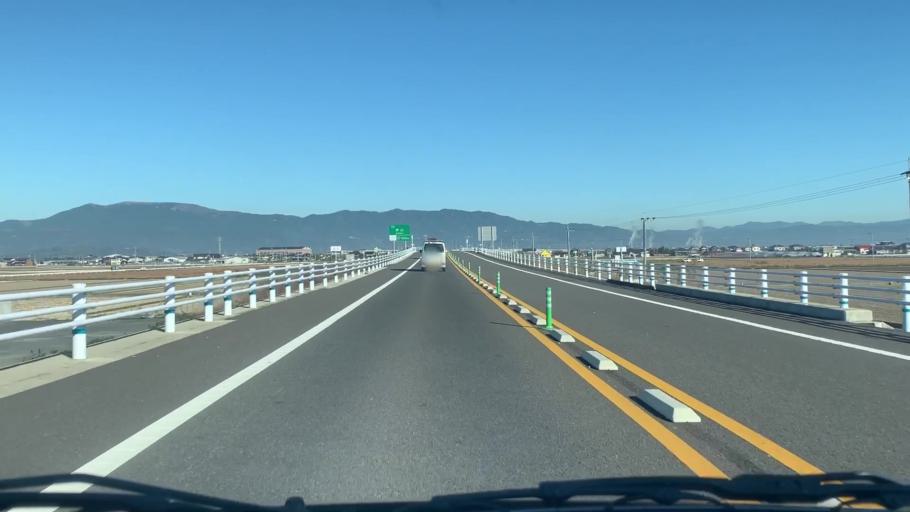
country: JP
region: Saga Prefecture
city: Saga-shi
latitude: 33.2127
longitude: 130.2146
